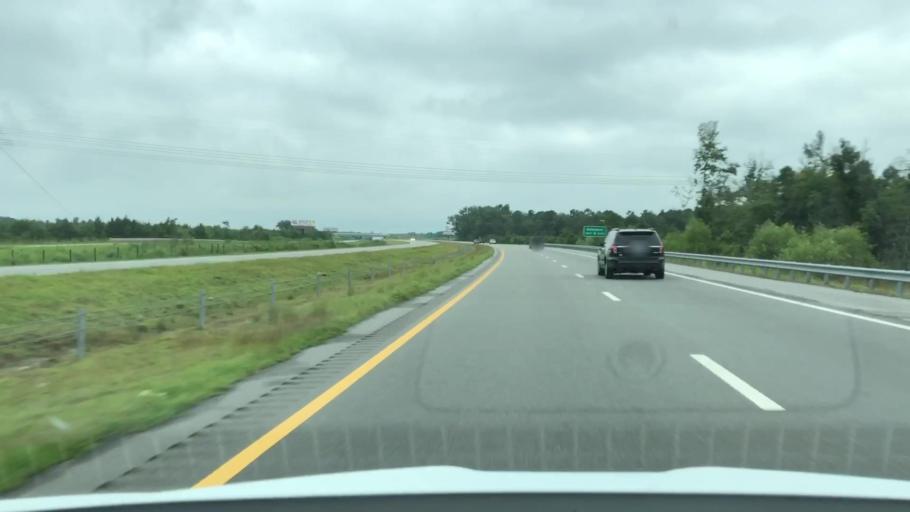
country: US
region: North Carolina
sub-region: Wayne County
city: Elroy
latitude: 35.3982
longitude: -77.8709
